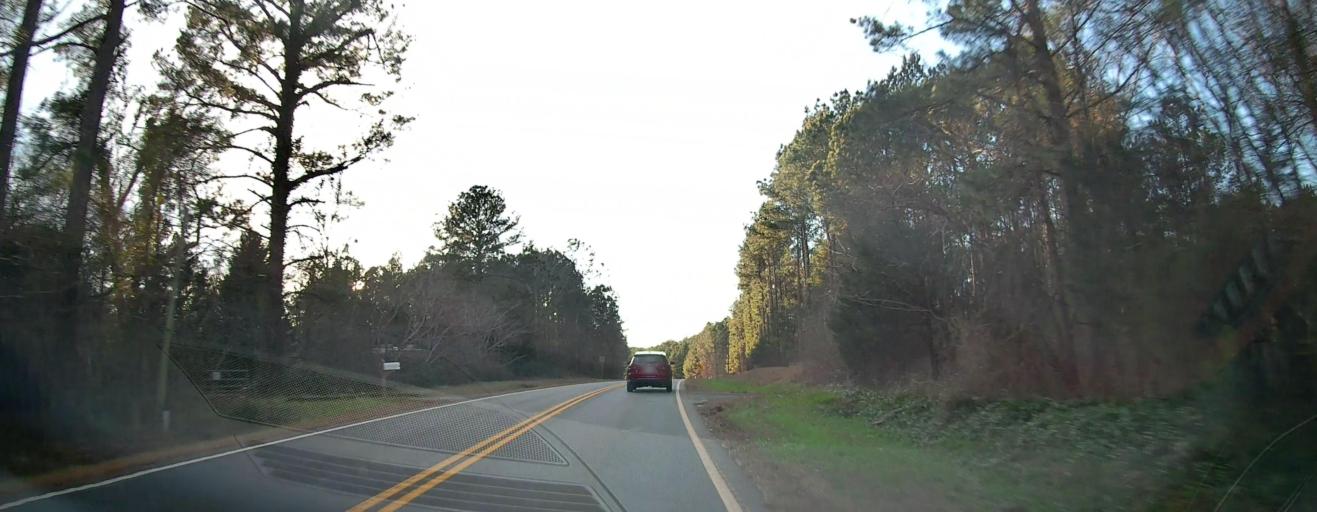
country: US
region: Georgia
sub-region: Talbot County
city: Sardis
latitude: 32.7252
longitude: -84.6307
